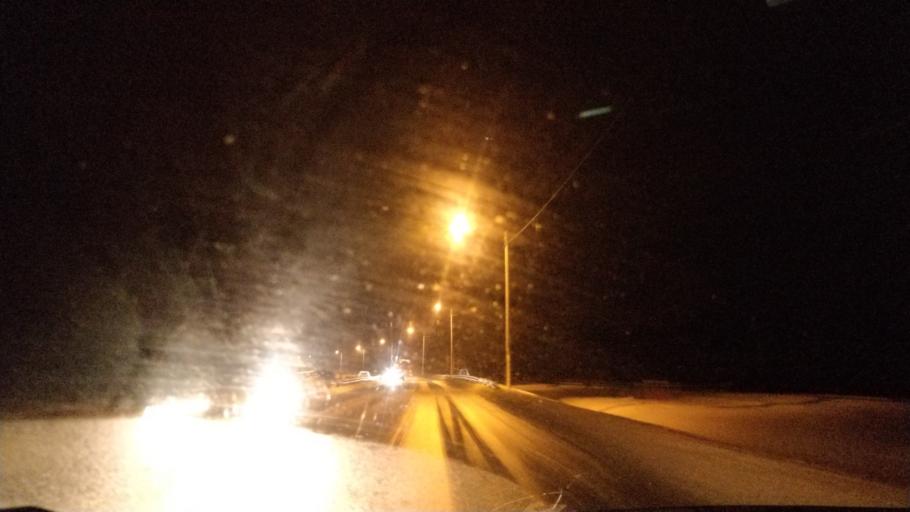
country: FI
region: Lapland
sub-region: Rovaniemi
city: Rovaniemi
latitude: 66.2867
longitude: 25.3434
